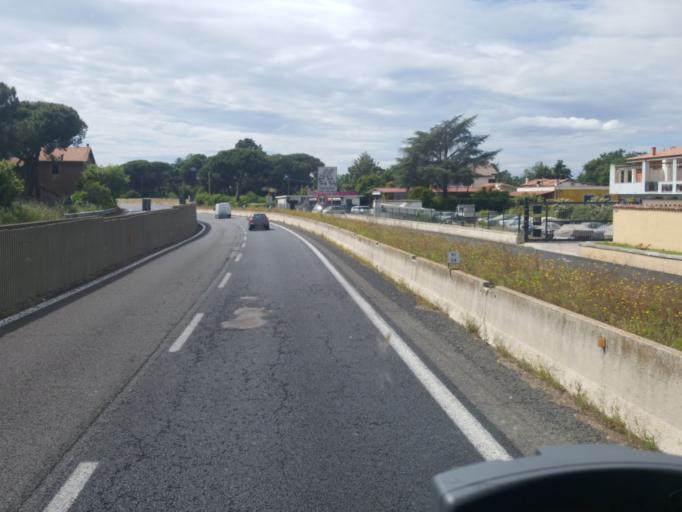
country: IT
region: Latium
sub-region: Citta metropolitana di Roma Capitale
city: Ara Nova
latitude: 41.9188
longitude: 12.2367
